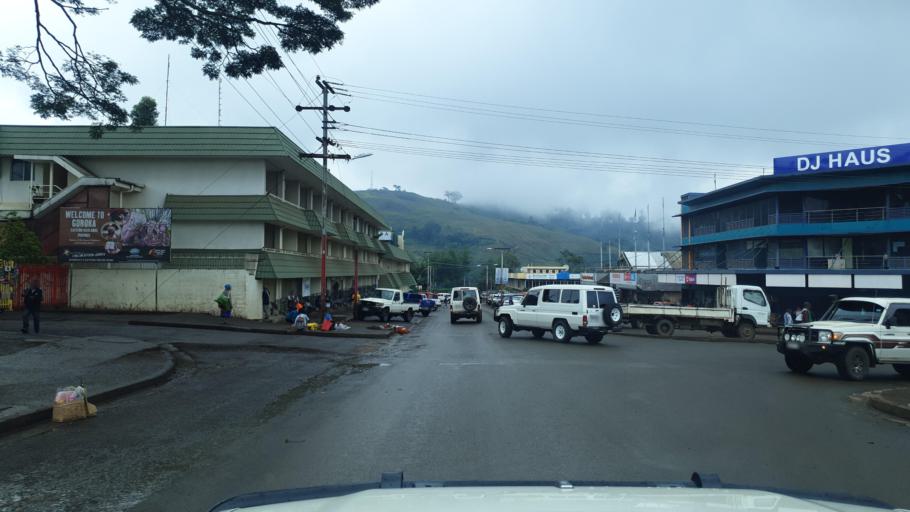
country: PG
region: Eastern Highlands
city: Goroka
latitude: -6.0730
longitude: 145.3942
